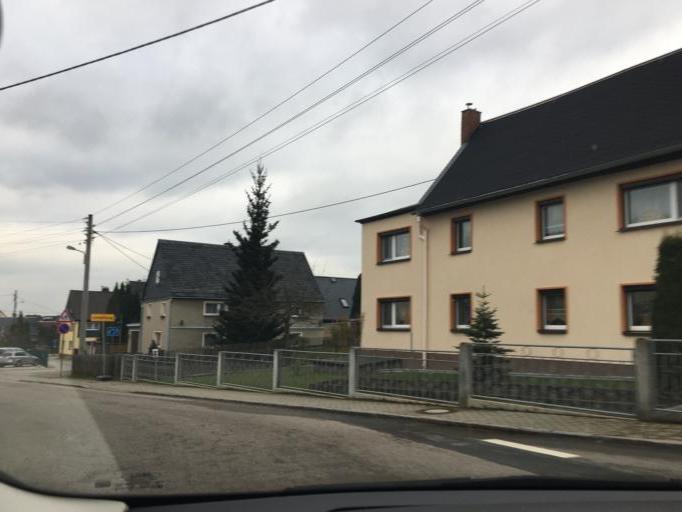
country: DE
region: Saxony
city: Hohenstein-Ernstthal
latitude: 50.8320
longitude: 12.7080
